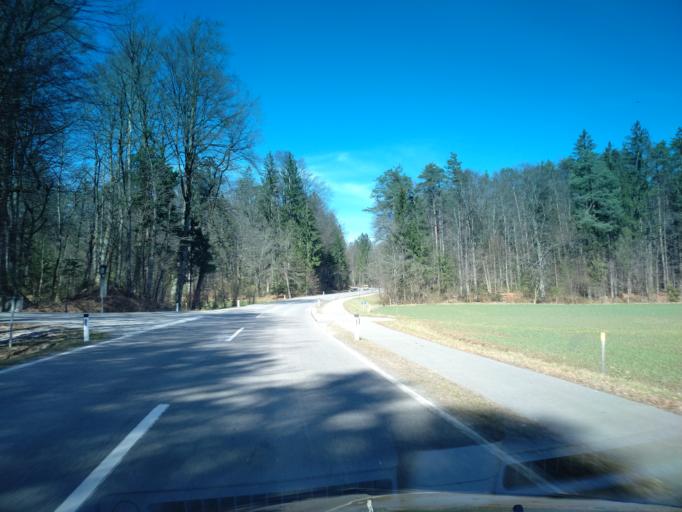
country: AT
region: Styria
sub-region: Politischer Bezirk Deutschlandsberg
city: Sankt Peter im Sulmtal
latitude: 46.7730
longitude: 15.2557
